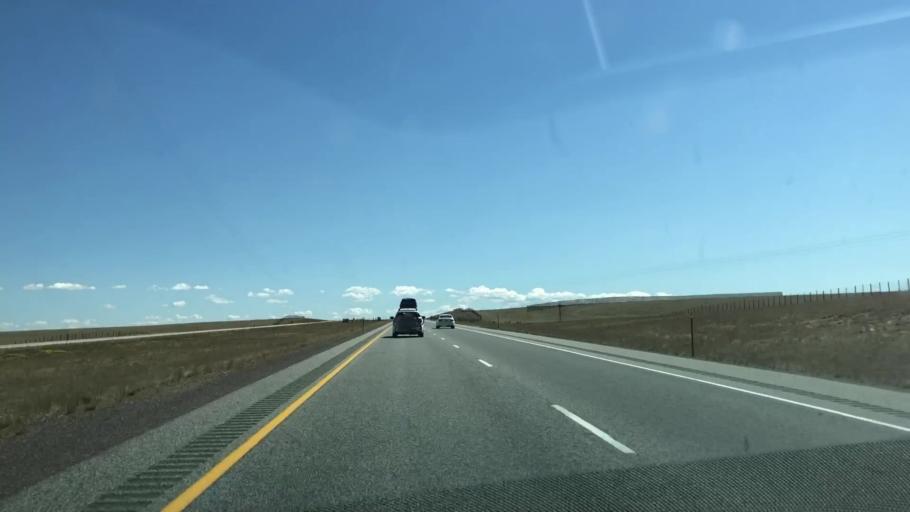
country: US
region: Wyoming
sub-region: Albany County
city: Laramie
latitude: 41.4756
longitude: -106.0085
